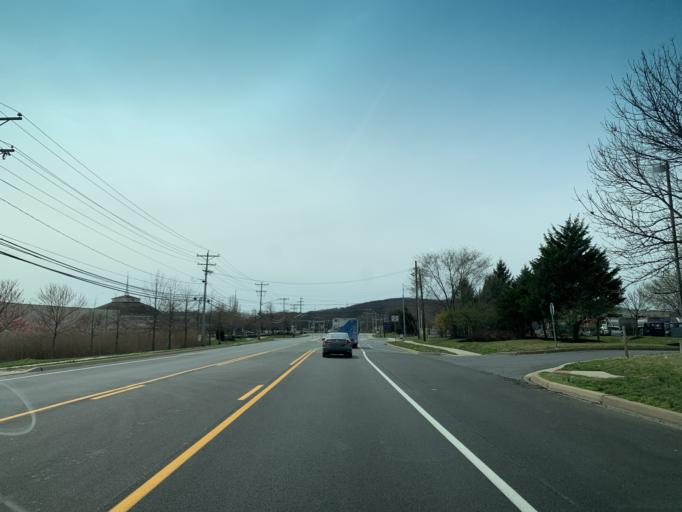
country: US
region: Delaware
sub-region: New Castle County
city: Brookside
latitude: 39.6430
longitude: -75.7271
